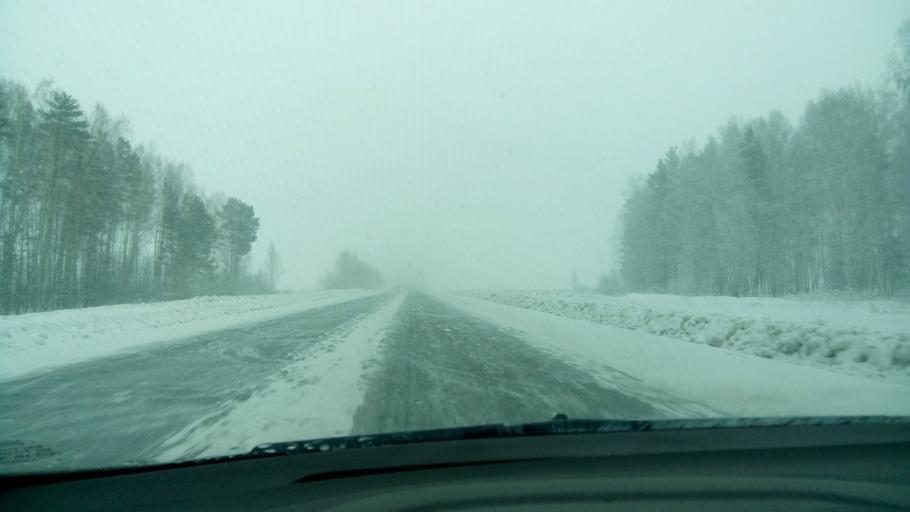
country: RU
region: Sverdlovsk
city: Beloyarskiy
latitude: 56.7727
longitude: 61.4972
